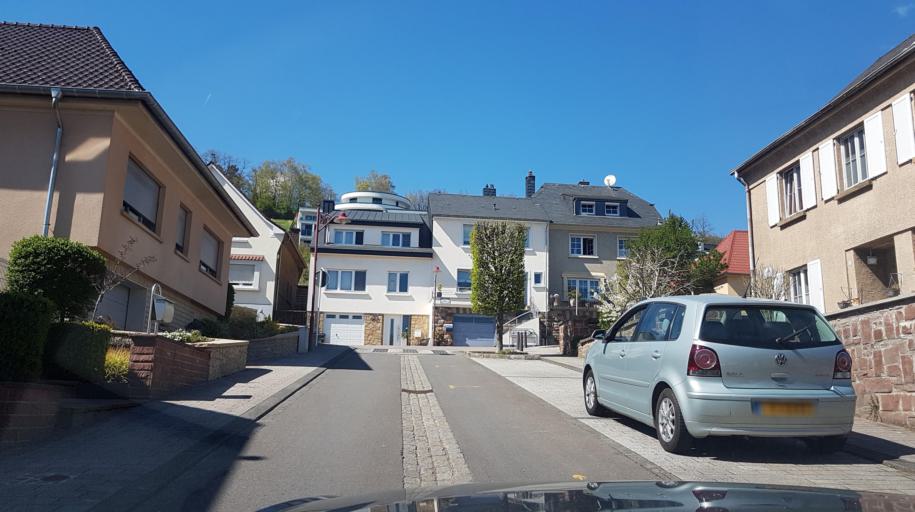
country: DE
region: Rheinland-Pfalz
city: Oberbillig
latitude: 49.7136
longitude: 6.4931
